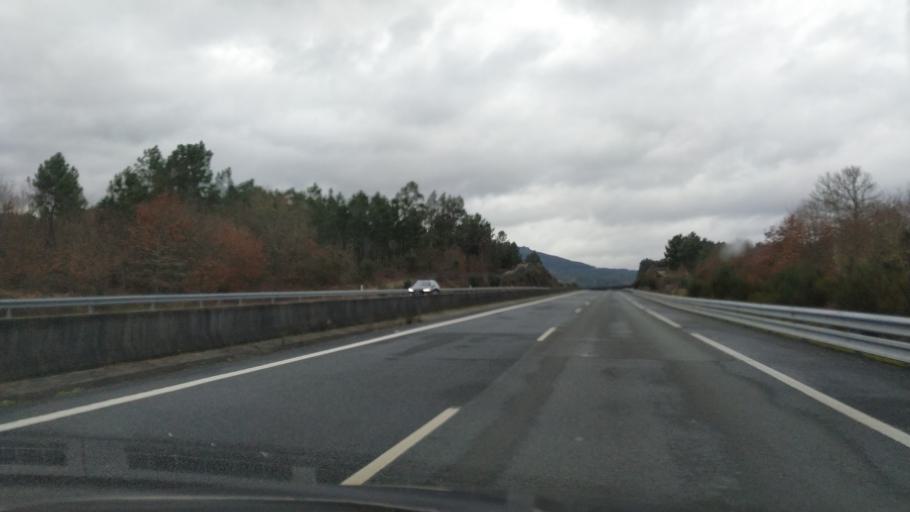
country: ES
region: Galicia
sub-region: Provincia de Ourense
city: Pinor
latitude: 42.4860
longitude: -8.0219
